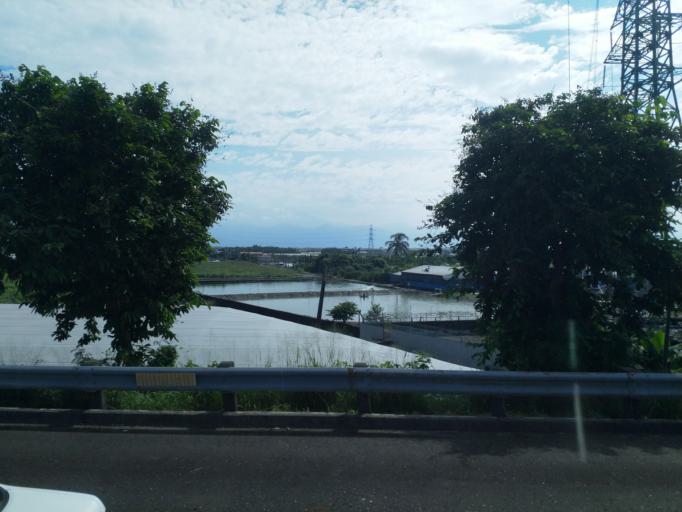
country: TW
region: Taiwan
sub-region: Pingtung
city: Pingtung
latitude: 22.8170
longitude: 120.4867
